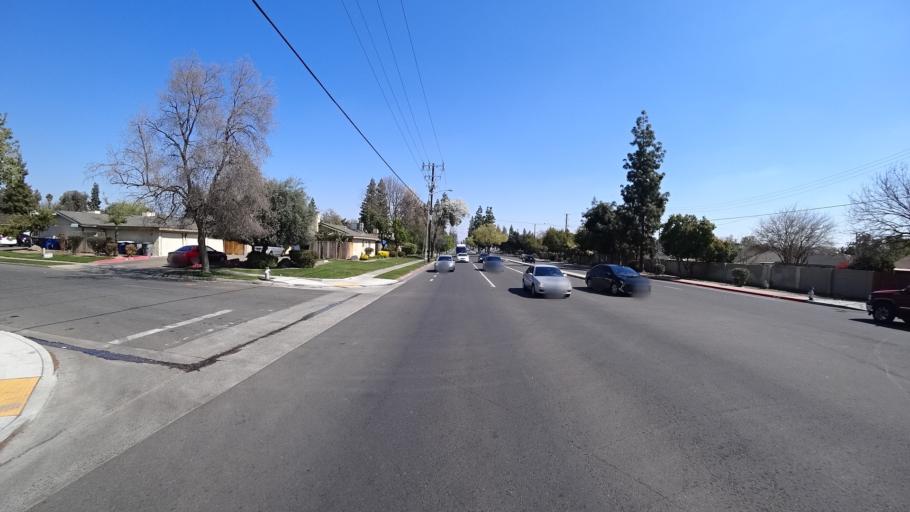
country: US
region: California
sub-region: Fresno County
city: West Park
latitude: 36.7938
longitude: -119.8484
